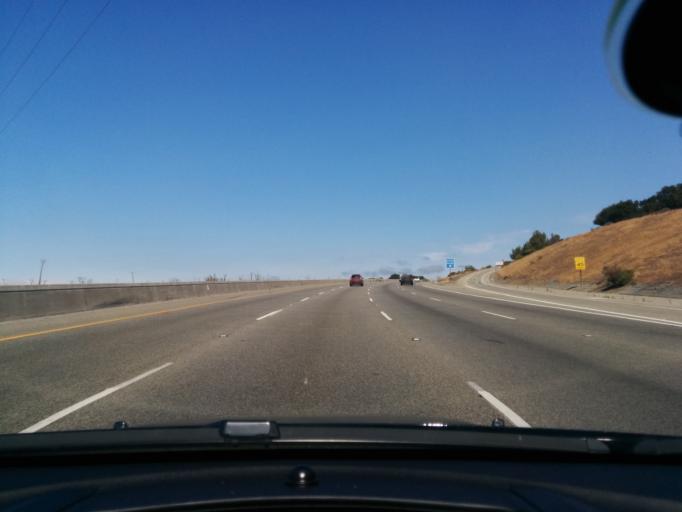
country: US
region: California
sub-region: San Mateo County
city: Emerald Lake Hills
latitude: 37.4740
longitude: -122.2972
